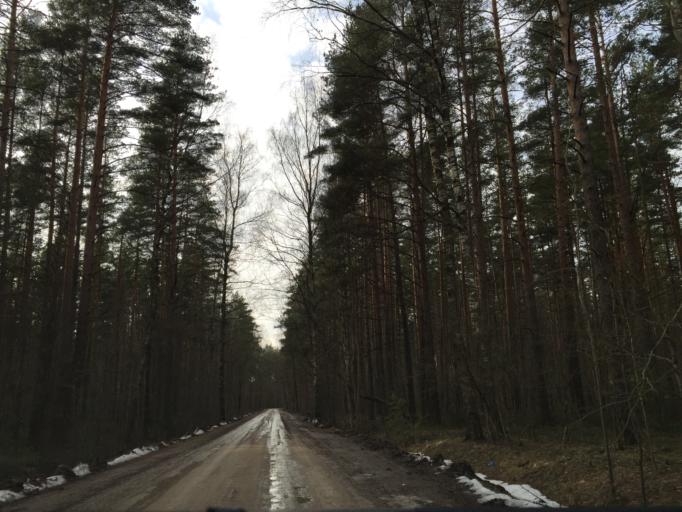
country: LV
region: Stopini
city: Ulbroka
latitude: 56.9220
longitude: 24.2979
